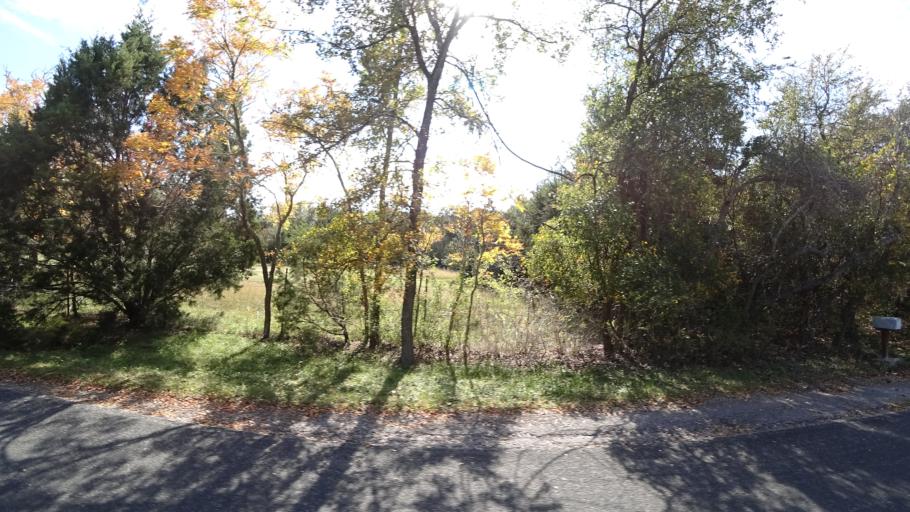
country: US
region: Texas
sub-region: Travis County
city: Barton Creek
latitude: 30.2247
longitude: -97.9265
